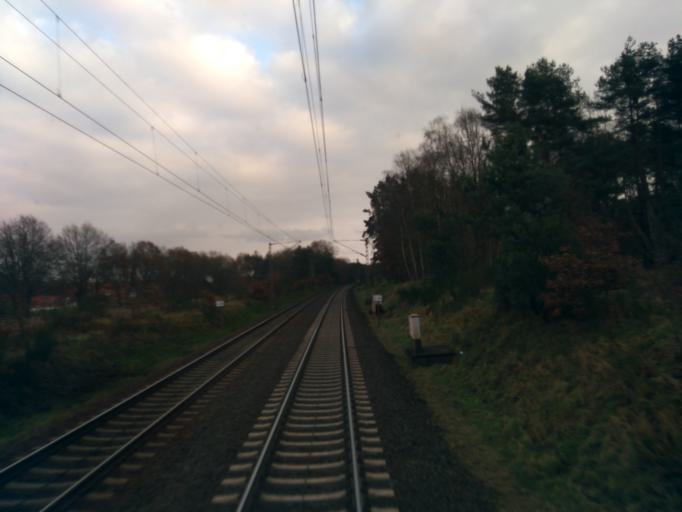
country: DE
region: Lower Saxony
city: Bienenbuttel
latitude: 53.1312
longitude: 10.5055
